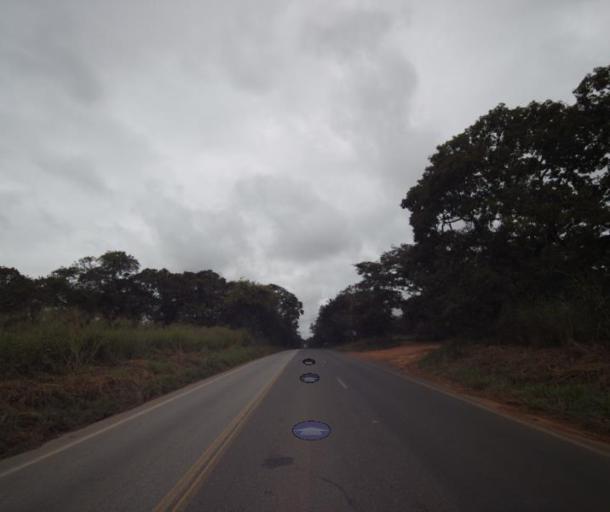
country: BR
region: Goias
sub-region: Uruacu
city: Uruacu
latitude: -14.5971
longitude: -49.1642
